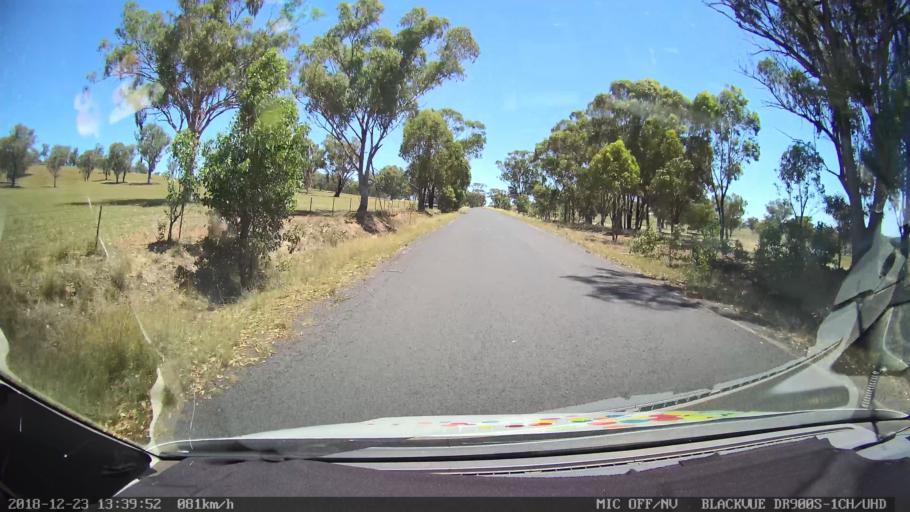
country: AU
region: New South Wales
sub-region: Armidale Dumaresq
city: Armidale
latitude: -30.4620
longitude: 151.1971
